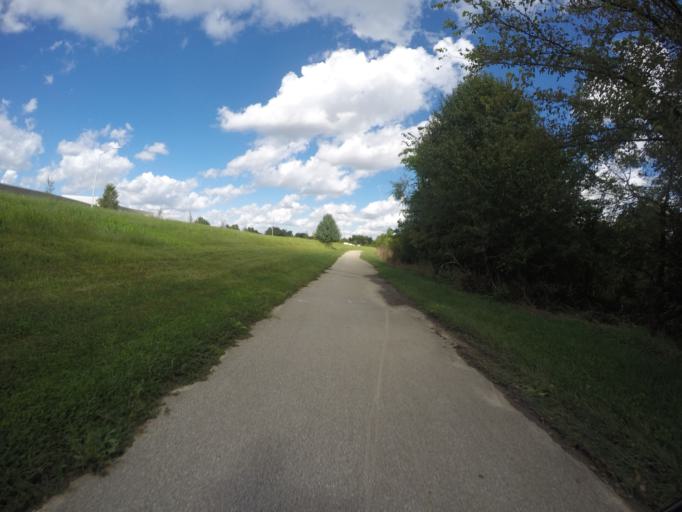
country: US
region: Kansas
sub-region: Johnson County
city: Lenexa
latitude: 38.9141
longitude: -94.7151
